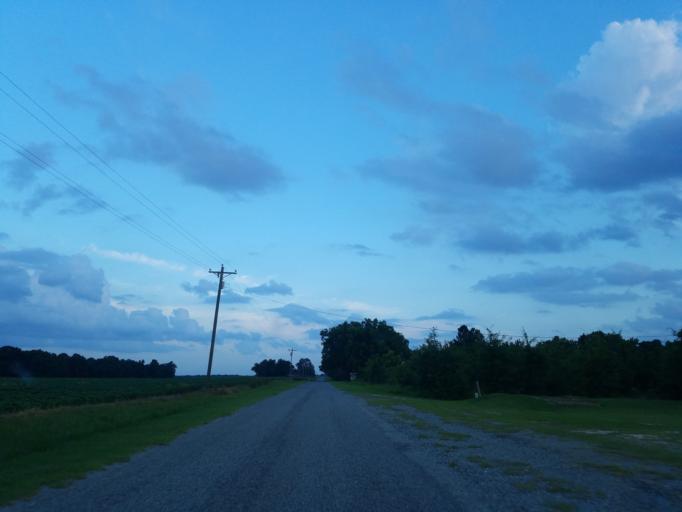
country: US
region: Georgia
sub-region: Dooly County
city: Unadilla
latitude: 32.1698
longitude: -83.7361
